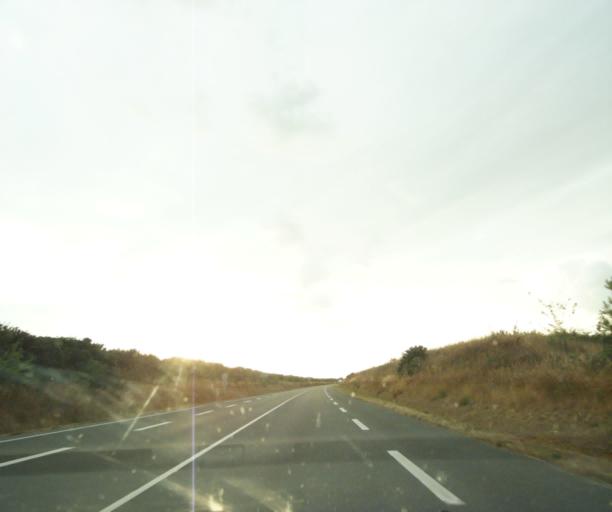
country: FR
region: Pays de la Loire
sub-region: Departement de la Vendee
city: Saint-Hilaire-de-Talmont
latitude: 46.4644
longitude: -1.6407
